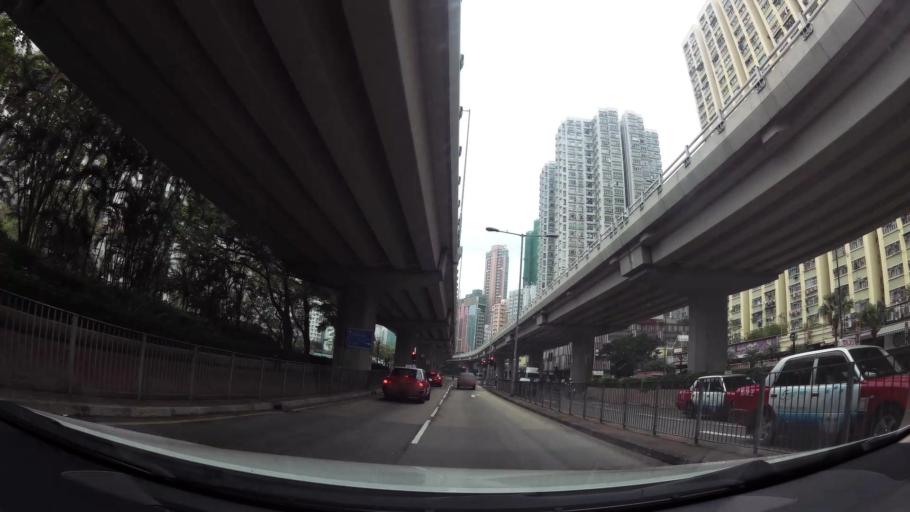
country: HK
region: Wanchai
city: Wan Chai
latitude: 22.2835
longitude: 114.2224
